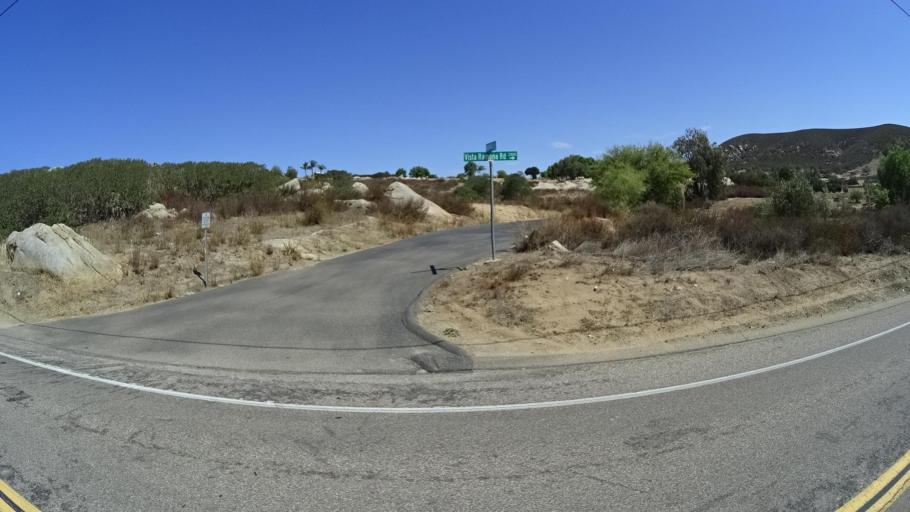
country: US
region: California
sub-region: San Diego County
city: San Diego Country Estates
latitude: 33.0345
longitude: -116.8202
